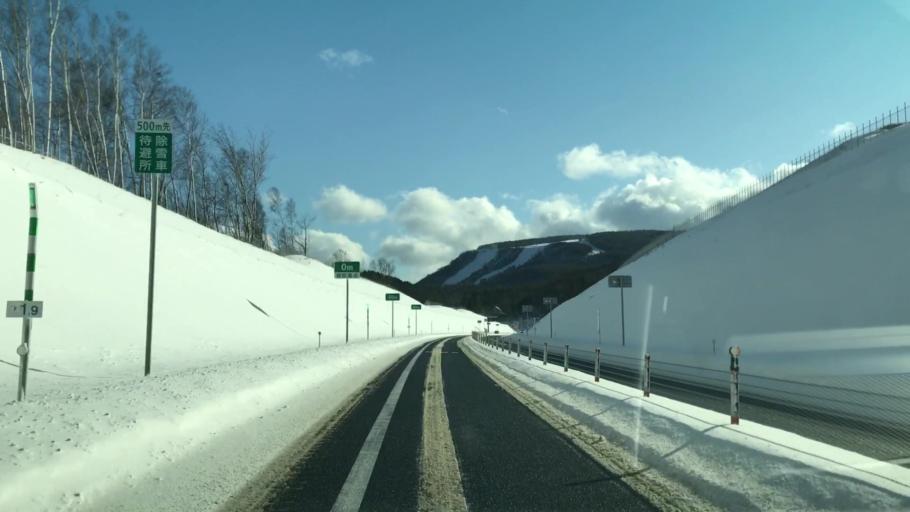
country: JP
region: Hokkaido
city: Otaru
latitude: 43.1929
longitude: 140.9556
